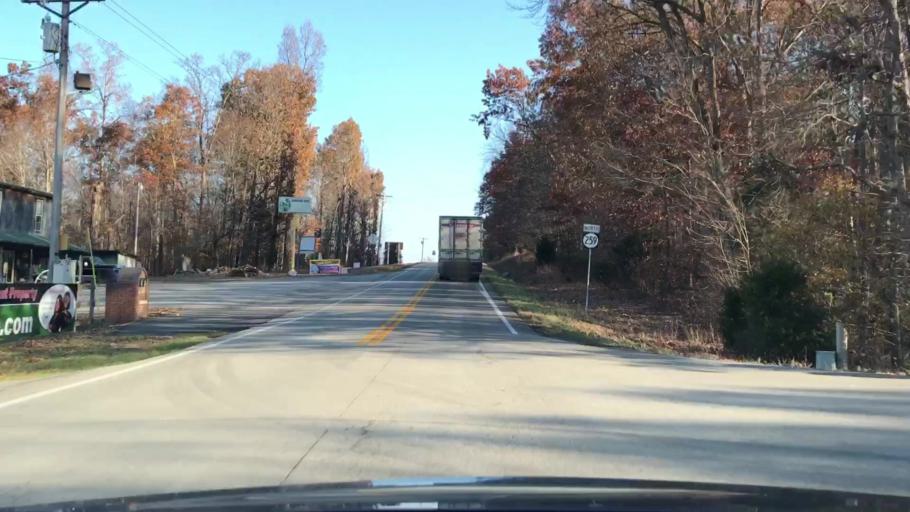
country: US
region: Kentucky
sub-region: Edmonson County
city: Brownsville
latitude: 37.3342
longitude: -86.2482
